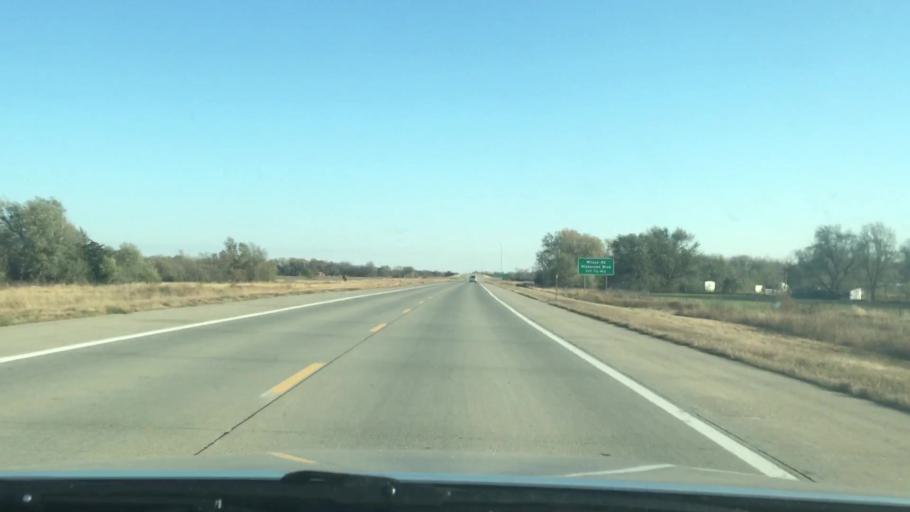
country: US
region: Kansas
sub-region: Reno County
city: Hutchinson
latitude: 38.0993
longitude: -98.0085
